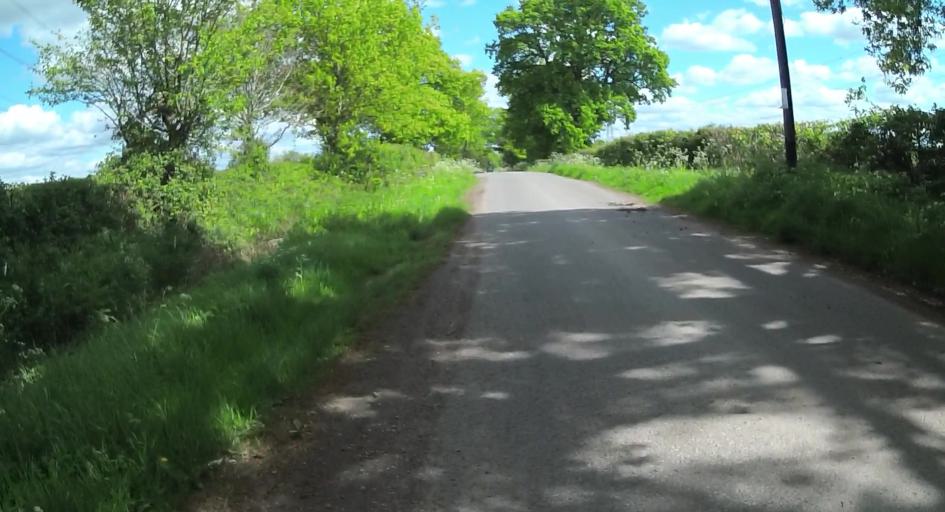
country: GB
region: England
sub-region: West Berkshire
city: Stratfield Mortimer
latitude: 51.3324
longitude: -1.0484
